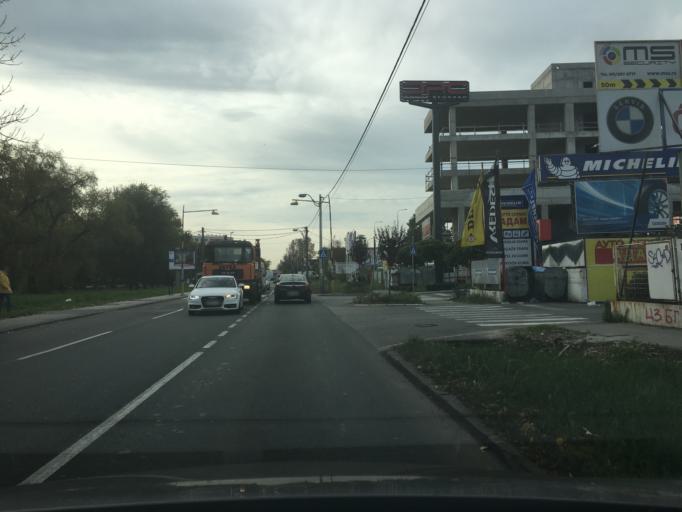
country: RS
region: Central Serbia
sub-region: Belgrade
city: Zemun
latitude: 44.8283
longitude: 20.3986
